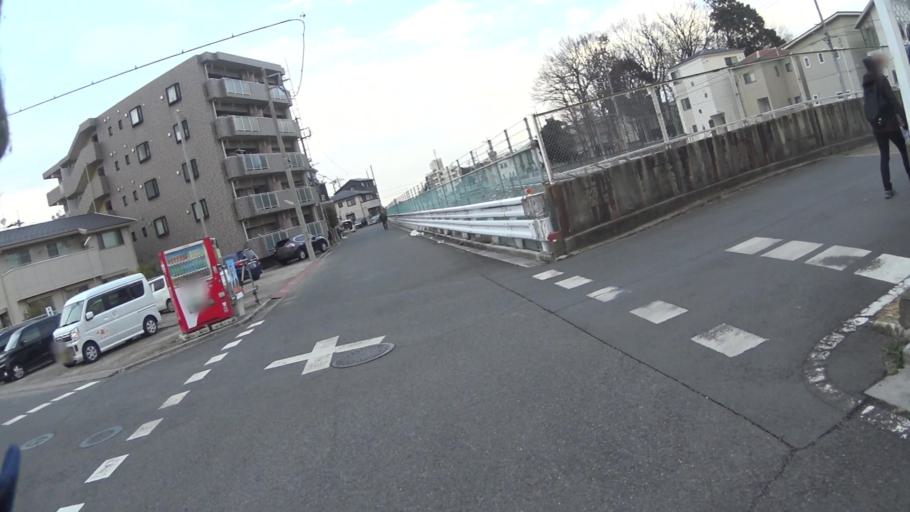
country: JP
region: Saitama
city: Shimotoda
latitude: 35.8607
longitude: 139.6962
